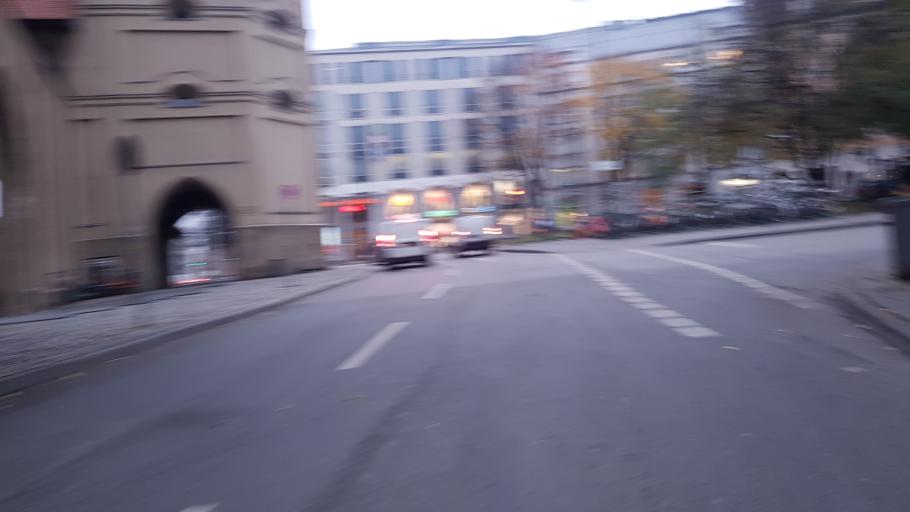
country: DE
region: Bavaria
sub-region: Upper Bavaria
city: Munich
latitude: 48.1352
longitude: 11.5814
